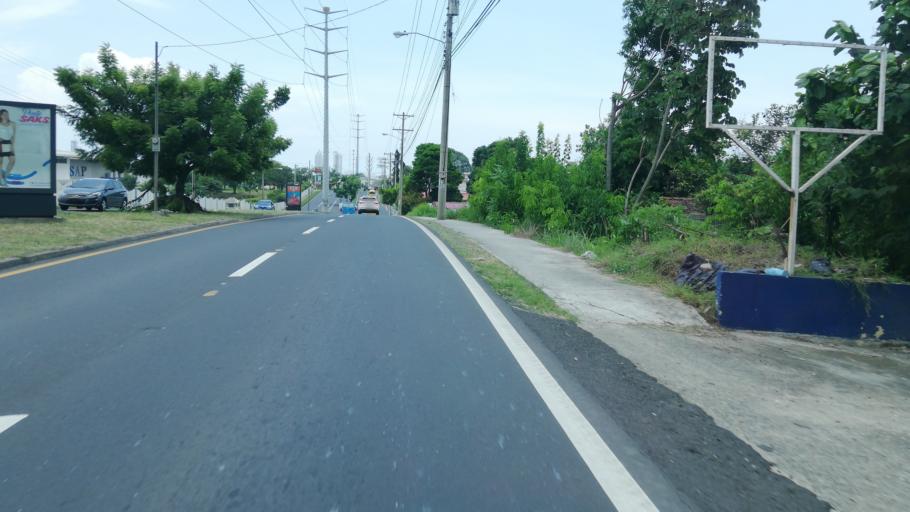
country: PA
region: Panama
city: San Miguelito
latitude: 9.0557
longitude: -79.4616
